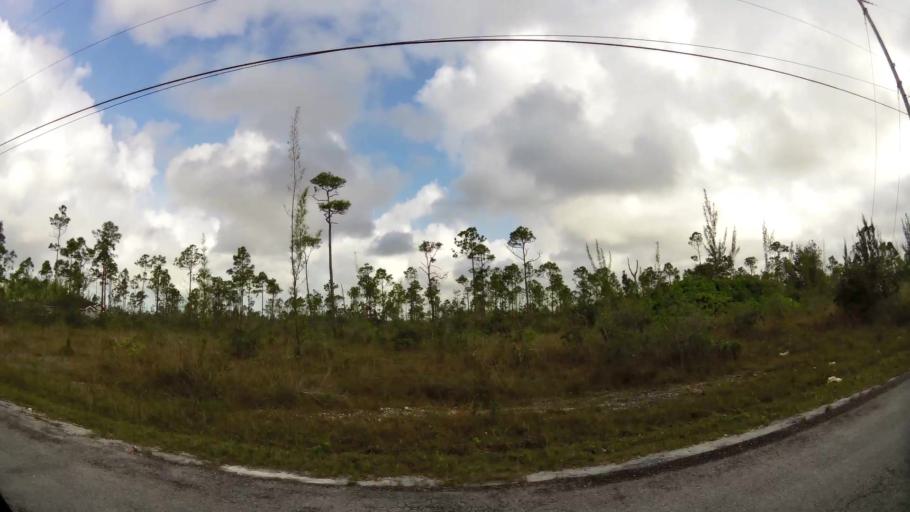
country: BS
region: Freeport
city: Lucaya
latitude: 26.5780
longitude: -78.5882
